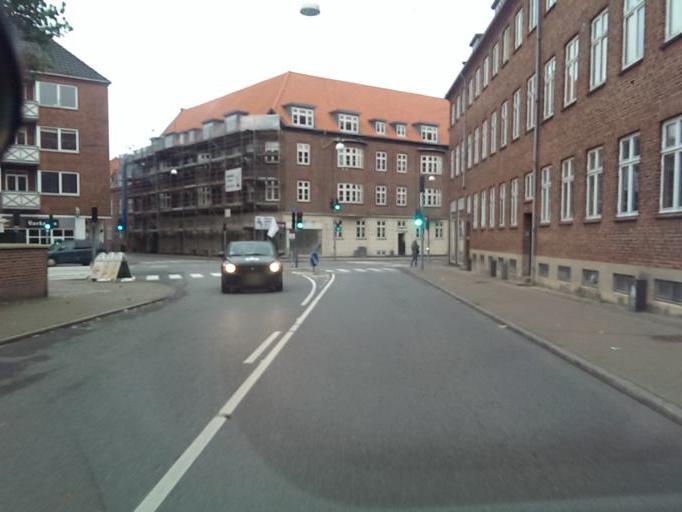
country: DK
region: South Denmark
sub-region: Esbjerg Kommune
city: Esbjerg
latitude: 55.4708
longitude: 8.4396
